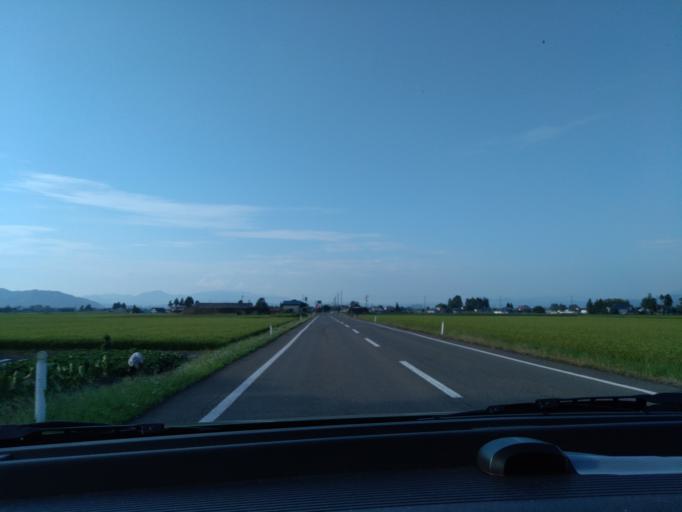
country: JP
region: Akita
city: Omagari
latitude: 39.4974
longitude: 140.5597
